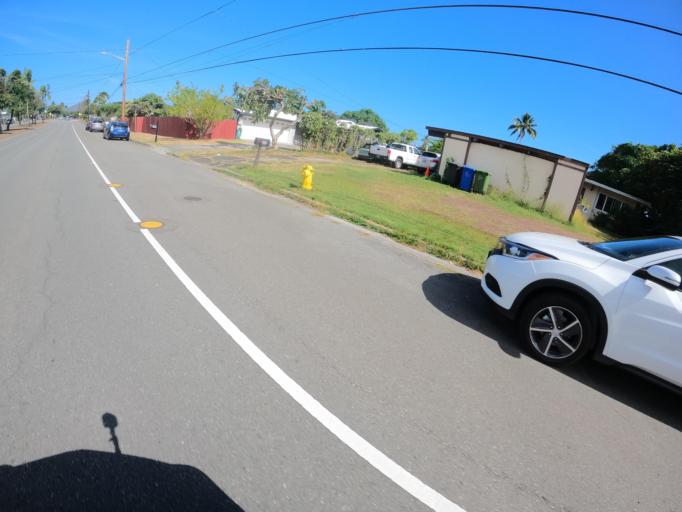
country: US
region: Hawaii
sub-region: Honolulu County
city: Kailua
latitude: 21.4177
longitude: -157.7500
